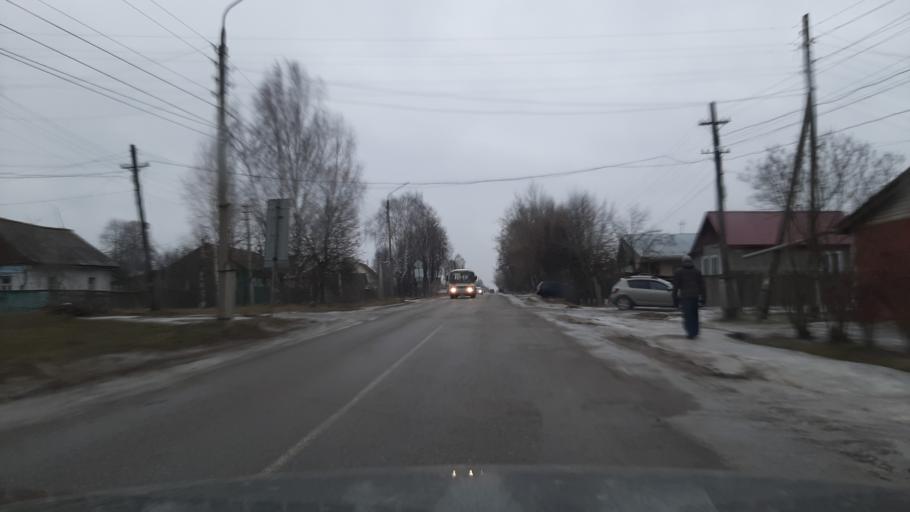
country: RU
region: Ivanovo
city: Shuya
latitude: 56.8730
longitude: 41.3529
